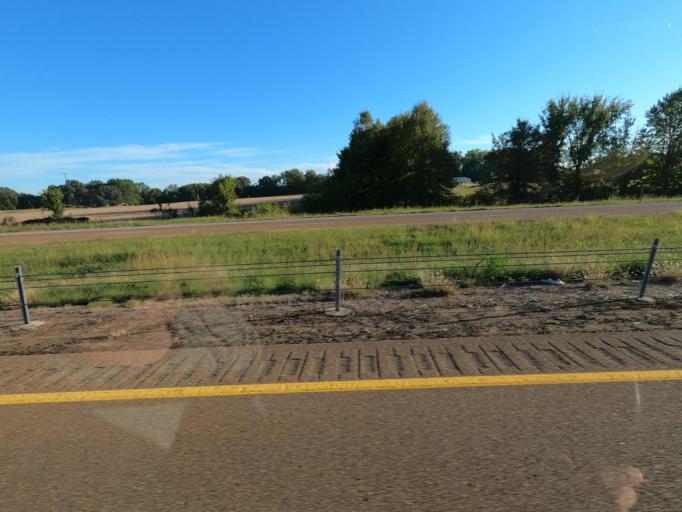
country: US
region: Tennessee
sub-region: Shelby County
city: Lakeland
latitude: 35.3088
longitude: -89.7871
